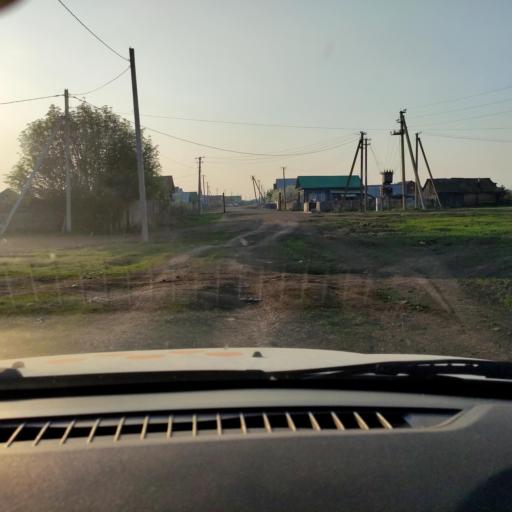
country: RU
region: Bashkortostan
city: Mikhaylovka
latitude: 54.9579
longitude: 55.8027
